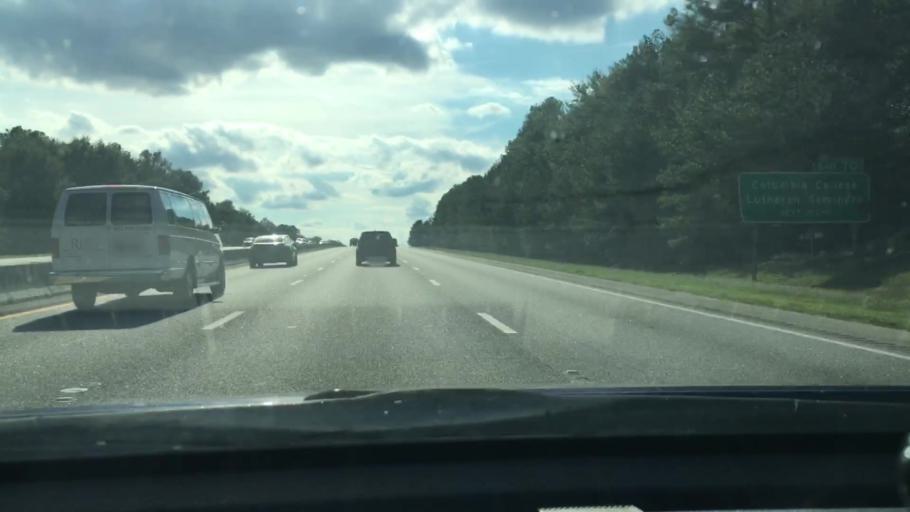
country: US
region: South Carolina
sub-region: Richland County
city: Forest Acres
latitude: 34.0696
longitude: -81.0157
